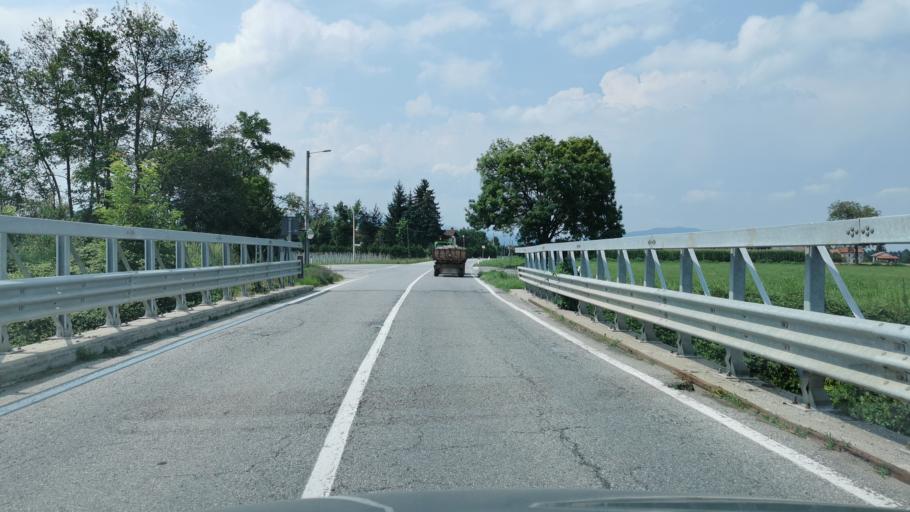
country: IT
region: Piedmont
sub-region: Provincia di Cuneo
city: Roata Rossi
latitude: 44.4360
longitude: 7.4986
